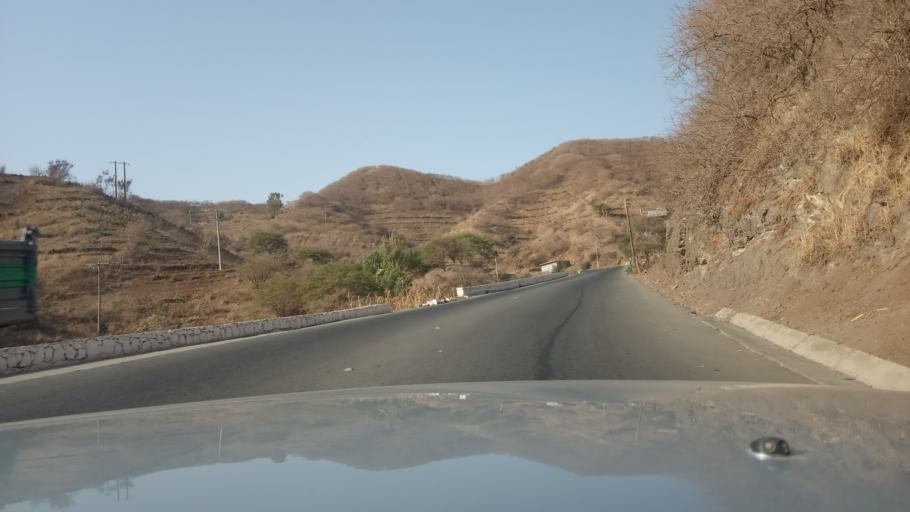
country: CV
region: Sao Domingos
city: Sao Domingos
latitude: 15.0409
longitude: -23.5765
